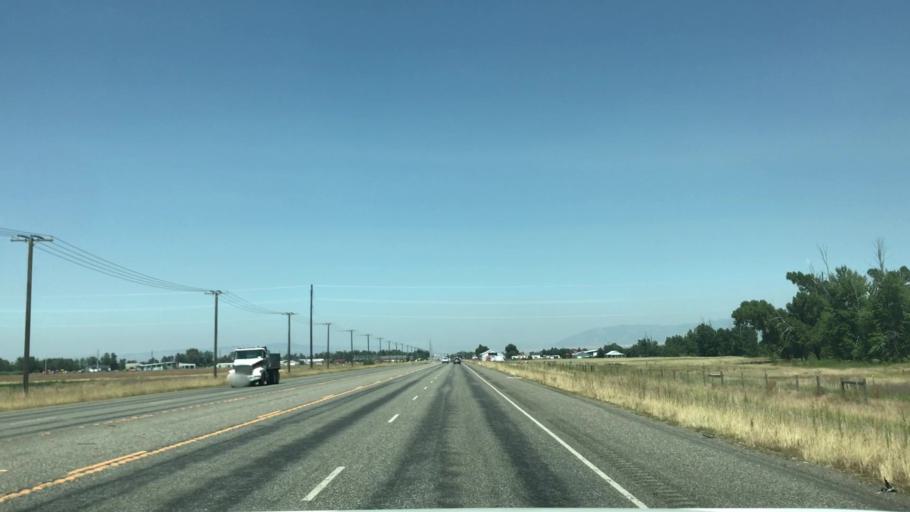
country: US
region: Montana
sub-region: Gallatin County
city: Four Corners
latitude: 45.6910
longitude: -111.1856
